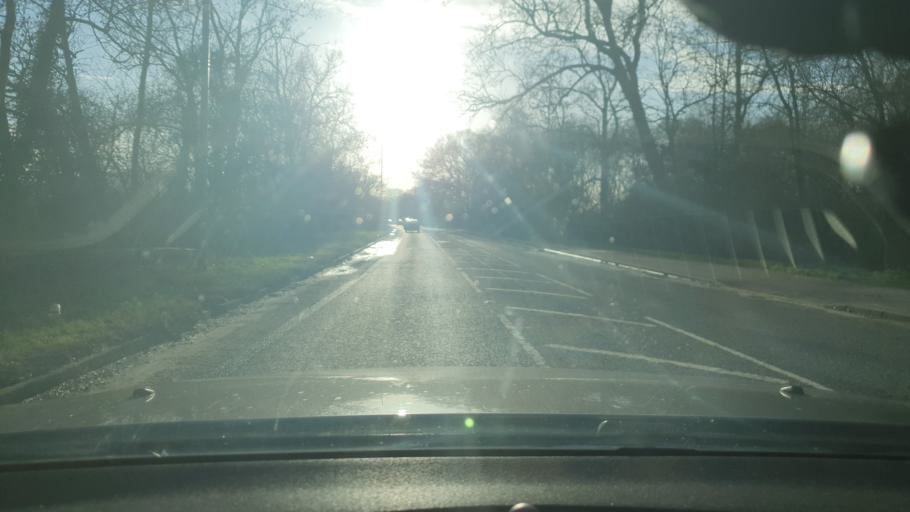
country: GB
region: England
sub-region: Wokingham
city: Charvil
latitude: 51.4838
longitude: -0.8775
